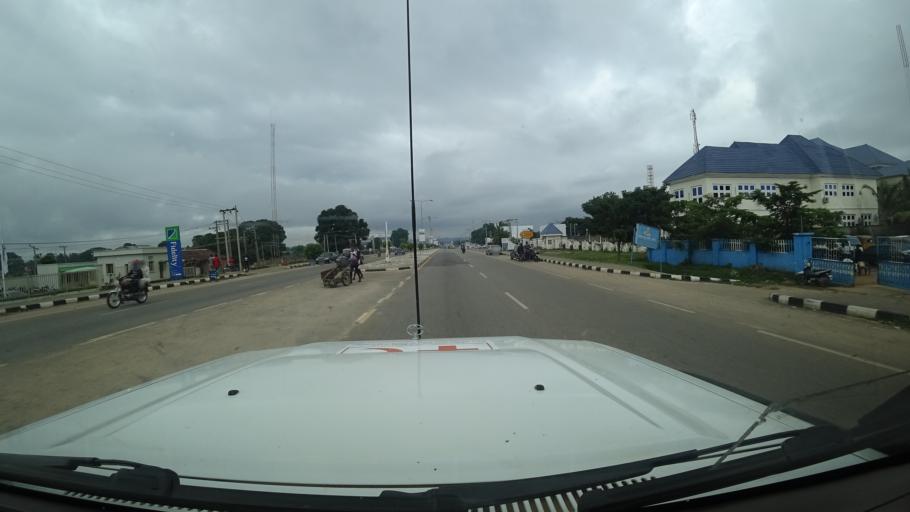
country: NG
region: Niger
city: Minna
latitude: 9.6060
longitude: 6.5552
